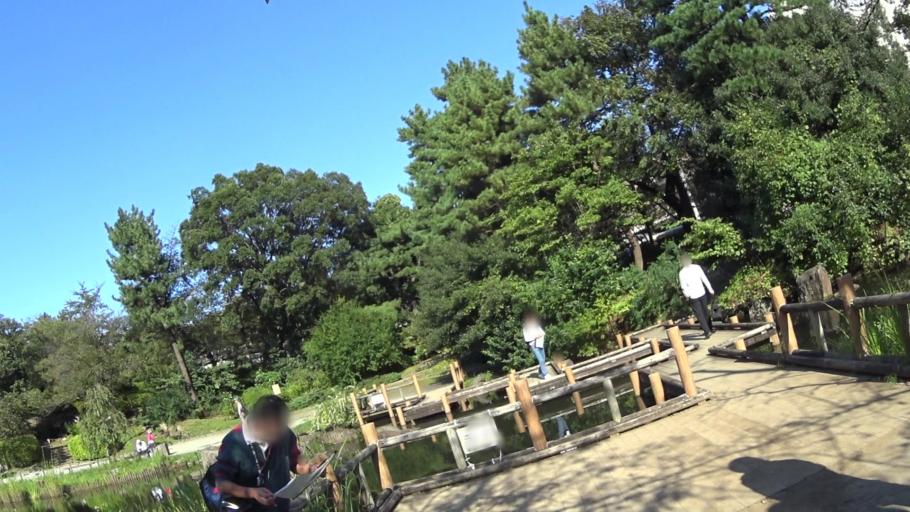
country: JP
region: Tokyo
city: Tokyo
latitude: 35.7210
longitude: 139.6752
